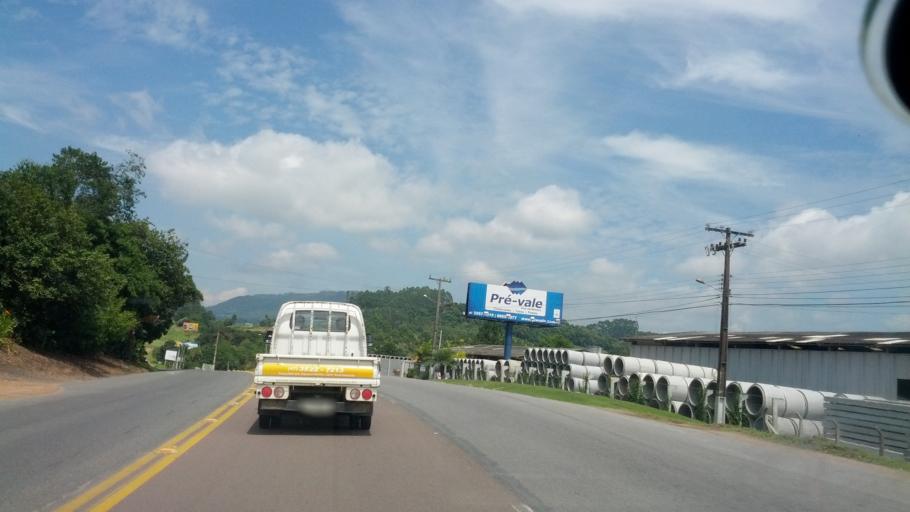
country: BR
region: Santa Catarina
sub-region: Ibirama
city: Ibirama
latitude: -27.1077
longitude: -49.5237
